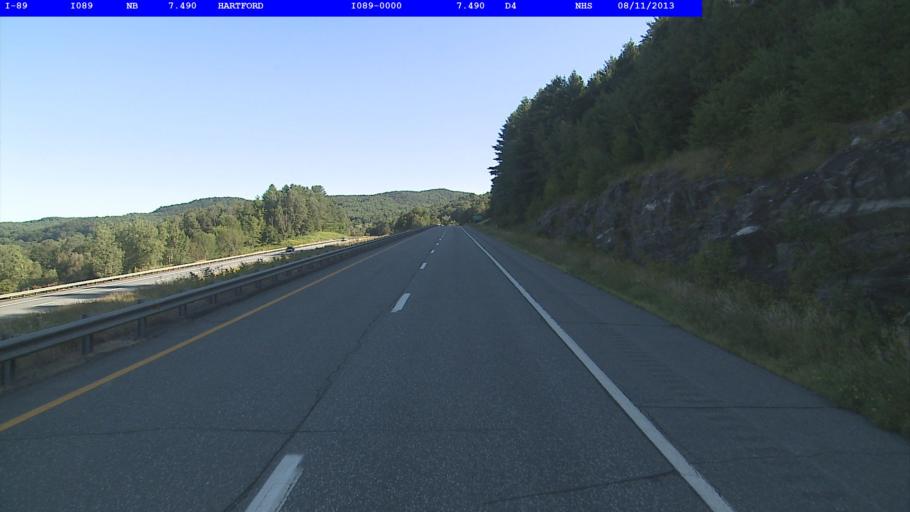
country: US
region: Vermont
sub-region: Windsor County
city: Wilder
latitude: 43.7125
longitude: -72.4133
